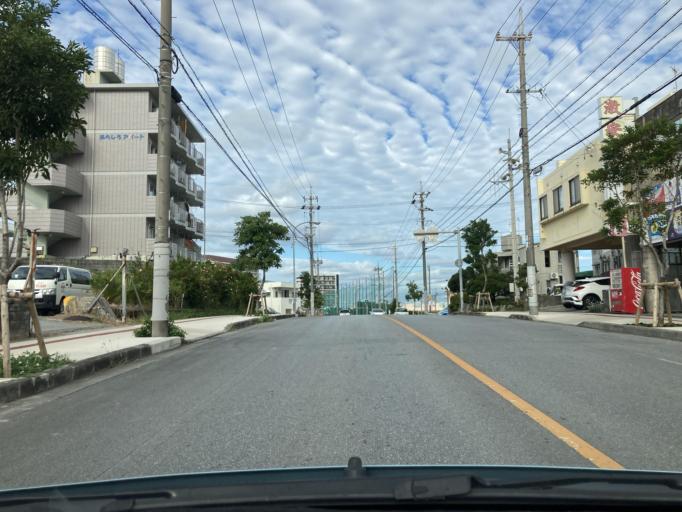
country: JP
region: Okinawa
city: Okinawa
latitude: 26.3374
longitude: 127.8204
